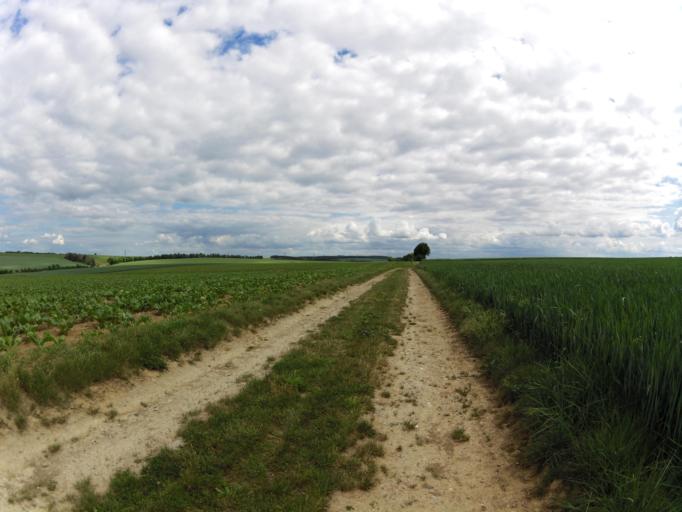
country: DE
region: Bavaria
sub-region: Regierungsbezirk Unterfranken
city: Gaukonigshofen
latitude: 49.6645
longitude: 10.0126
